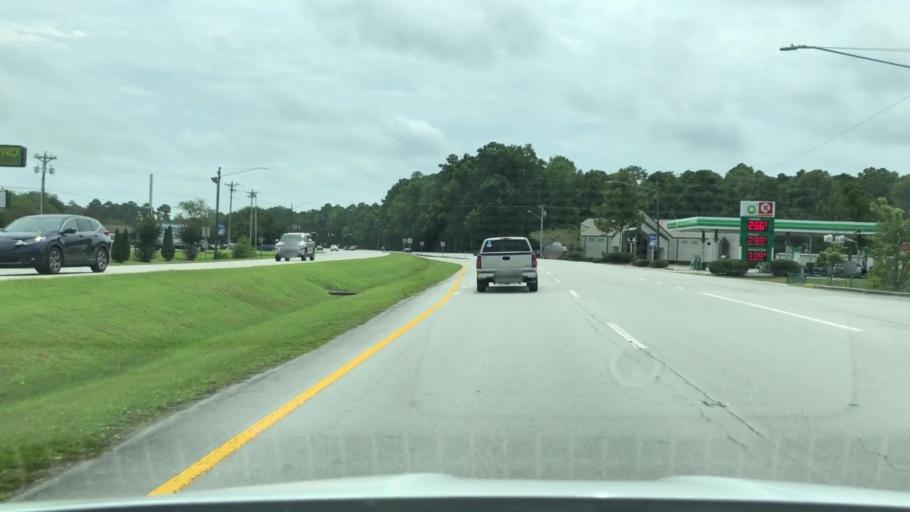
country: US
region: North Carolina
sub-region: Craven County
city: Havelock
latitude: 34.8585
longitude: -76.8967
